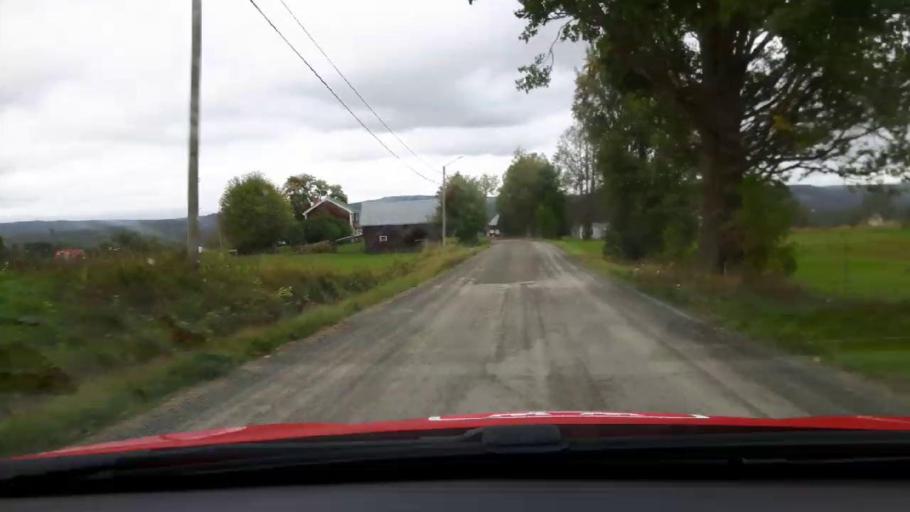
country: SE
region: Jaemtland
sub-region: Bergs Kommun
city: Hoverberg
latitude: 62.8520
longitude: 14.3429
